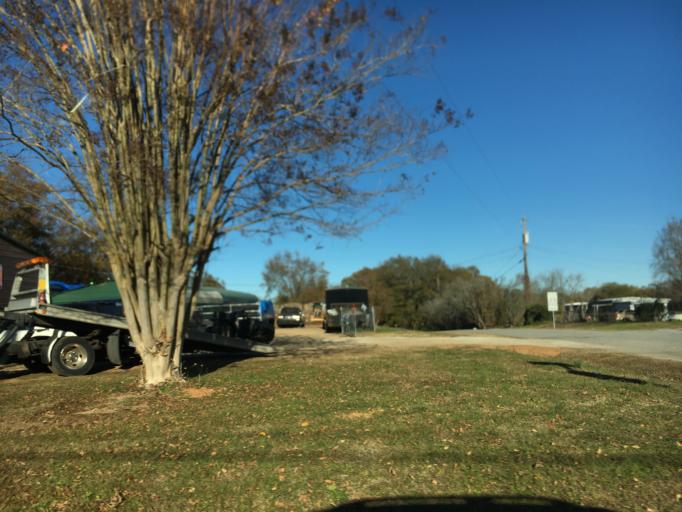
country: US
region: South Carolina
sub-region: Spartanburg County
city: Duncan
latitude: 34.9457
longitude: -82.1552
